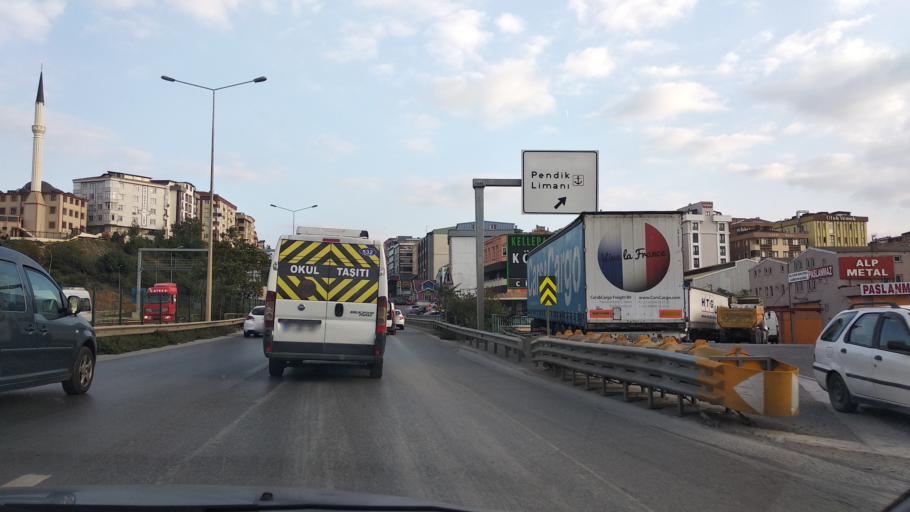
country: TR
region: Istanbul
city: Pendik
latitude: 40.8636
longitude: 29.2759
